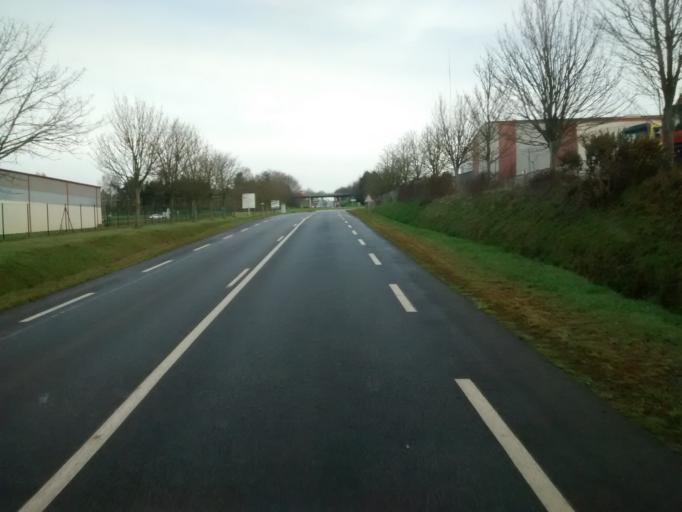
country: FR
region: Brittany
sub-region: Departement du Morbihan
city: Malestroit
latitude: 47.8484
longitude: -2.4181
